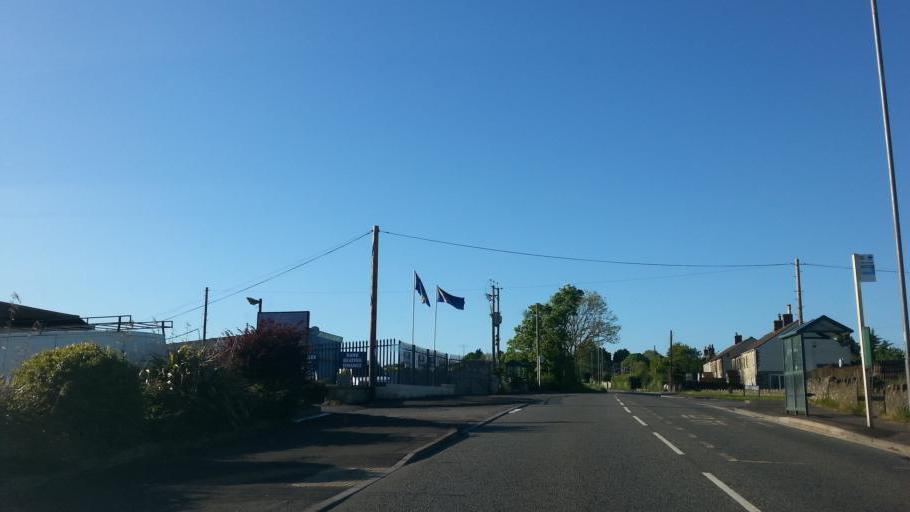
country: GB
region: England
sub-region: Bath and North East Somerset
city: Clutton
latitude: 51.3320
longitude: -2.5479
